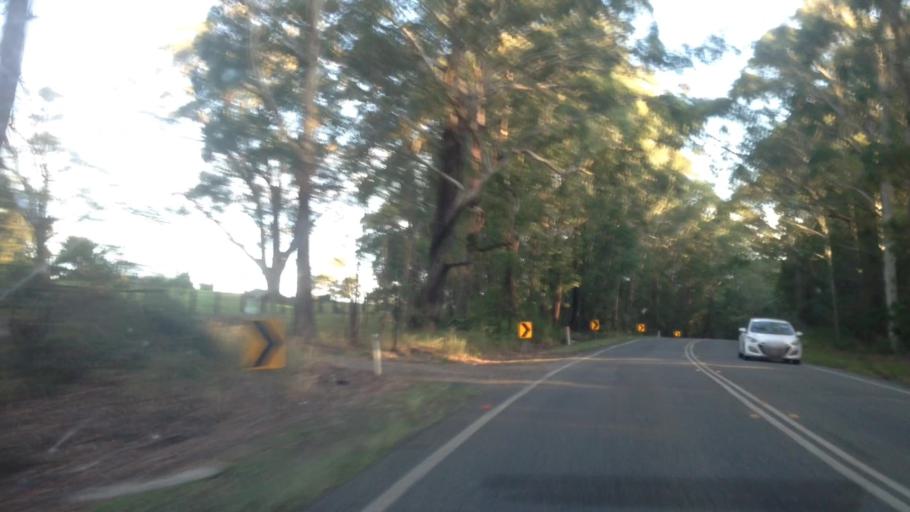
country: AU
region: New South Wales
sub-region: Lake Macquarie Shire
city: Cooranbong
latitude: -32.9782
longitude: 151.4836
